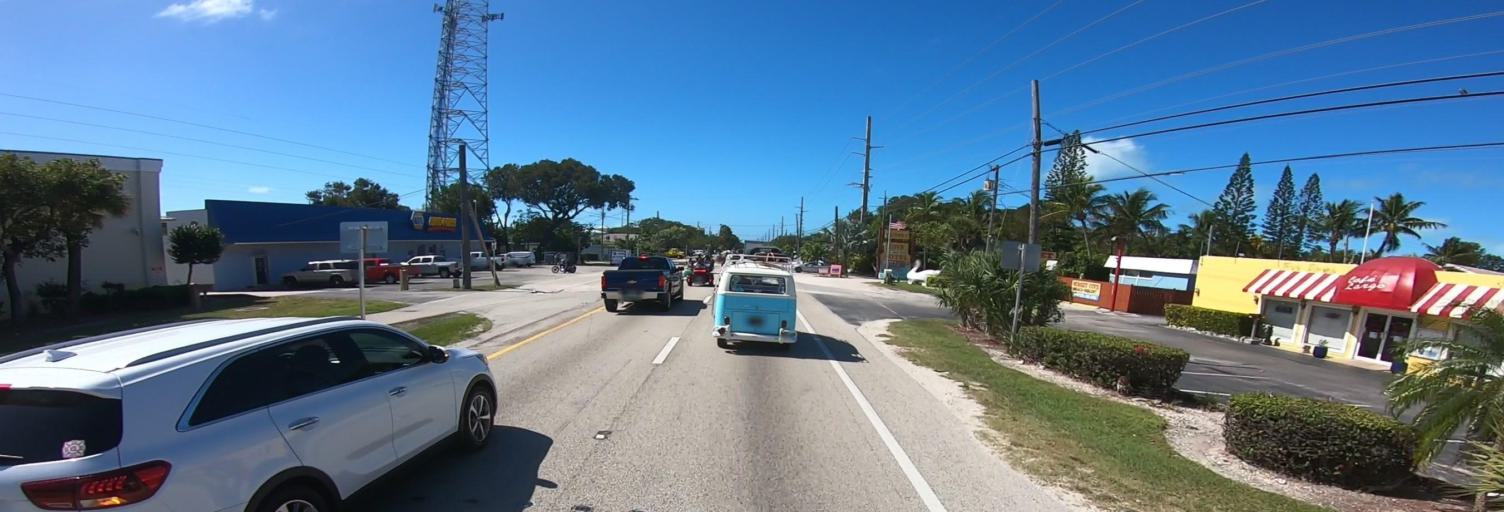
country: US
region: Florida
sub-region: Monroe County
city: Key Largo
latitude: 25.0932
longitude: -80.4427
